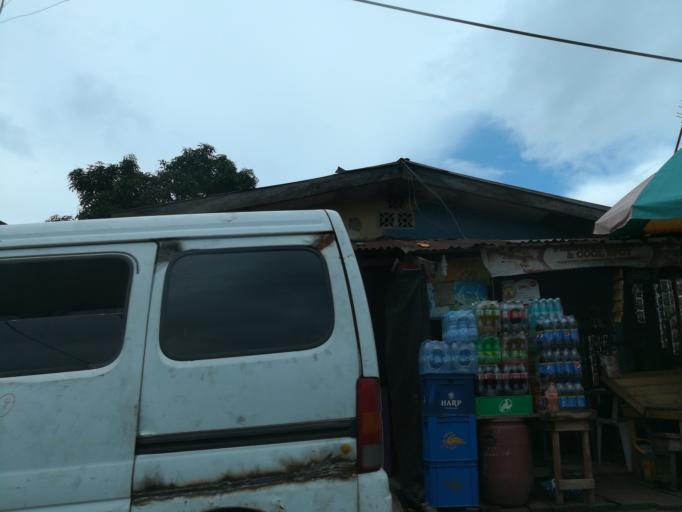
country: NG
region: Lagos
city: Agege
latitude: 6.6126
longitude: 3.3222
